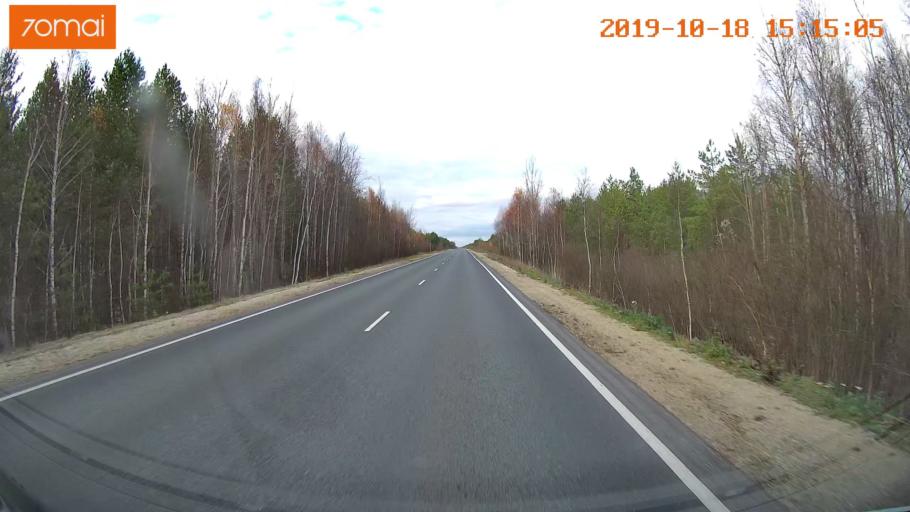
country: RU
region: Vladimir
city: Gus'-Khrustal'nyy
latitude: 55.6131
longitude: 40.7216
